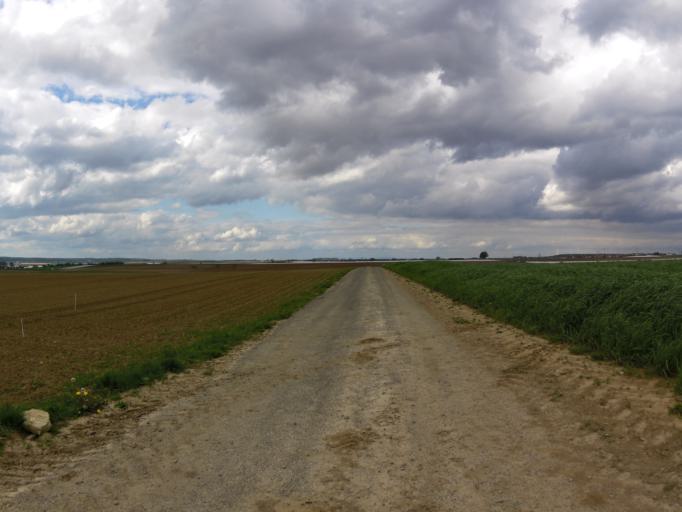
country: DE
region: Bavaria
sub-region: Regierungsbezirk Unterfranken
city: Oberpleichfeld
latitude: 49.8594
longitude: 10.0792
